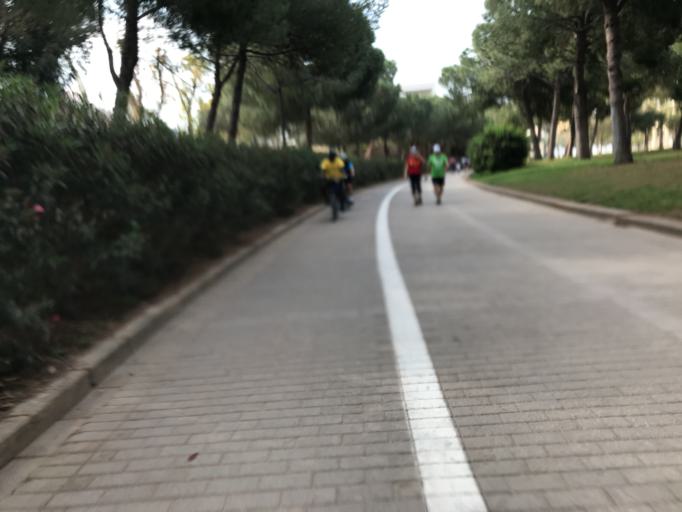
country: ES
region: Valencia
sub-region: Provincia de Valencia
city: Valencia
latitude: 39.4677
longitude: -0.3614
